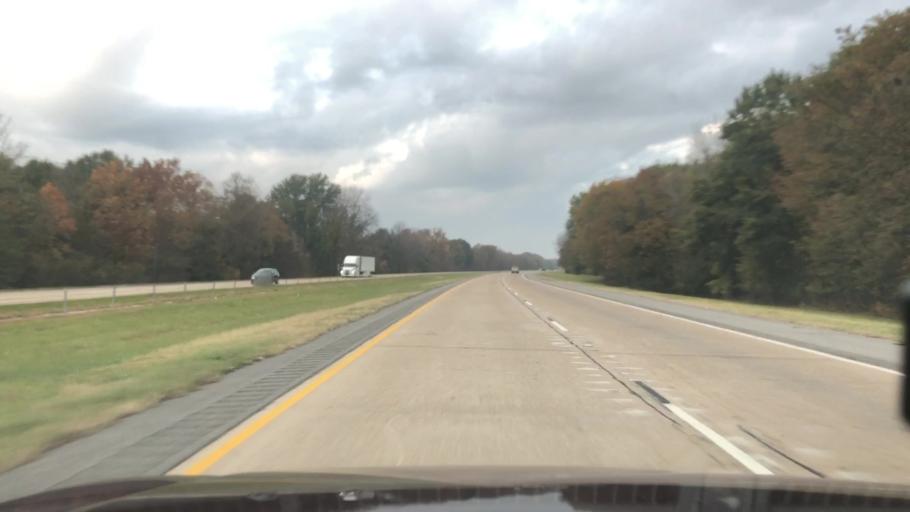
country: US
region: Louisiana
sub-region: Madison Parish
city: Tallulah
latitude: 32.3371
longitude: -91.0630
